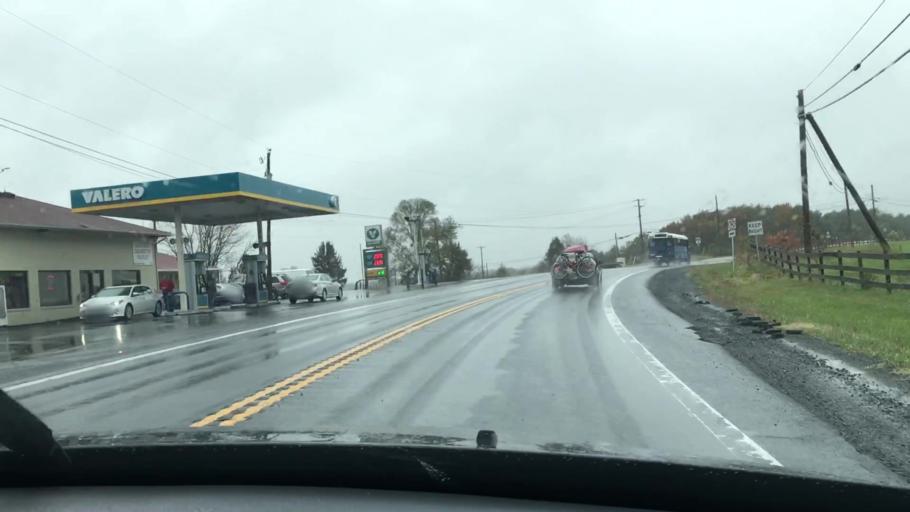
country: US
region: Maryland
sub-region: Frederick County
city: Point of Rocks
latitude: 39.2499
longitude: -77.5303
